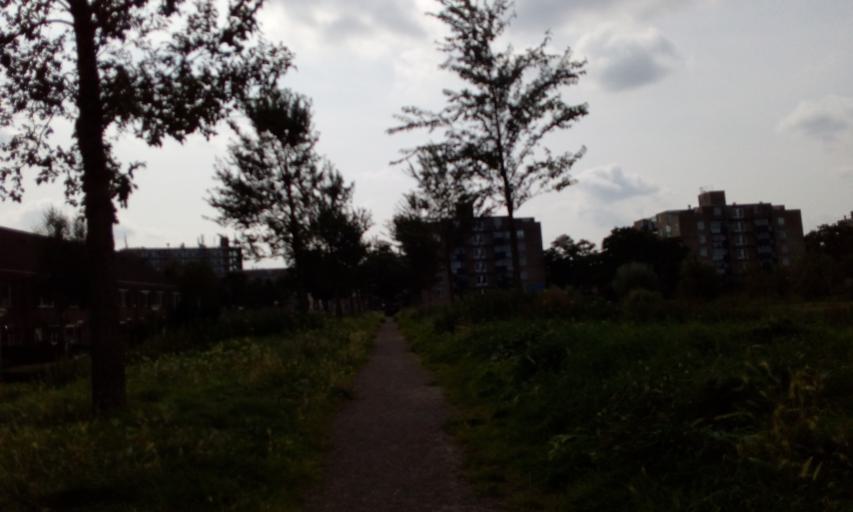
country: NL
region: South Holland
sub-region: Gemeente Capelle aan den IJssel
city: Capelle aan den IJssel
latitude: 51.9679
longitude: 4.5703
